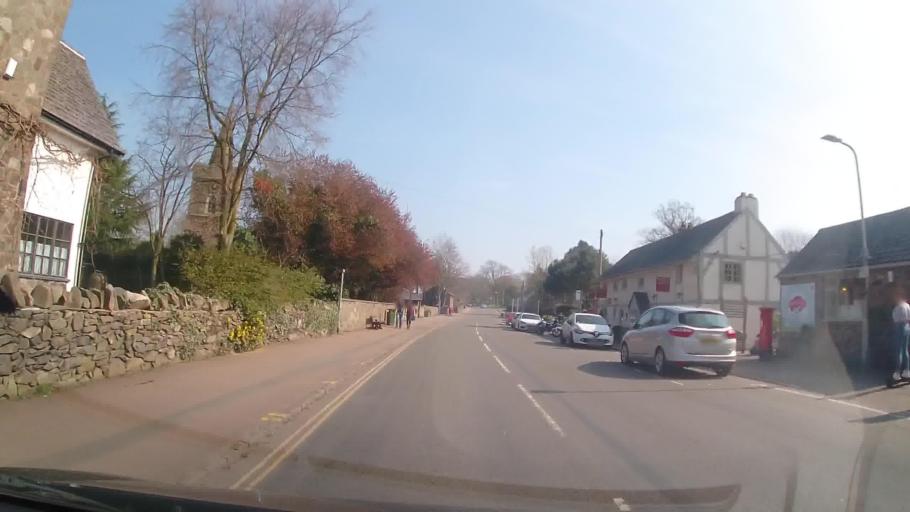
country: GB
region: England
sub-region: Leicestershire
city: Anstey
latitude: 52.6832
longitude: -1.2300
